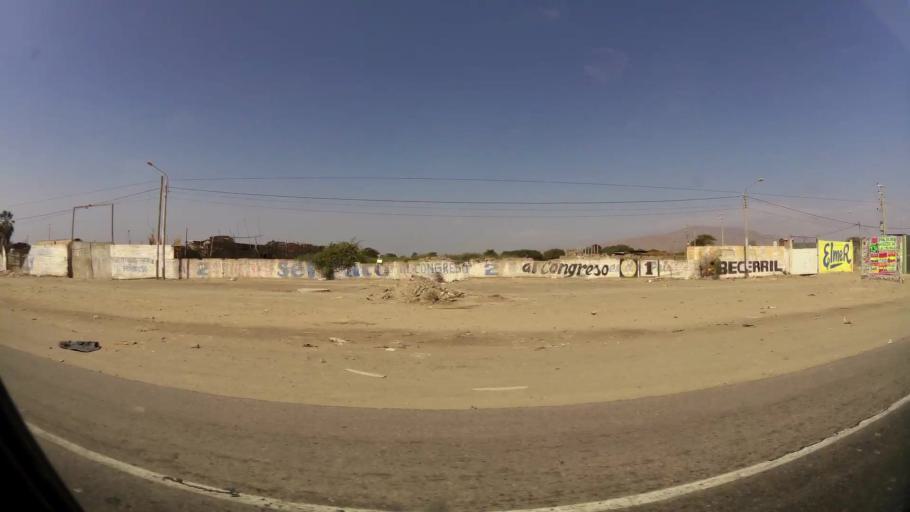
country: PE
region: Lambayeque
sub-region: Provincia de Chiclayo
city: Reque
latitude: -6.8215
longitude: -79.8294
